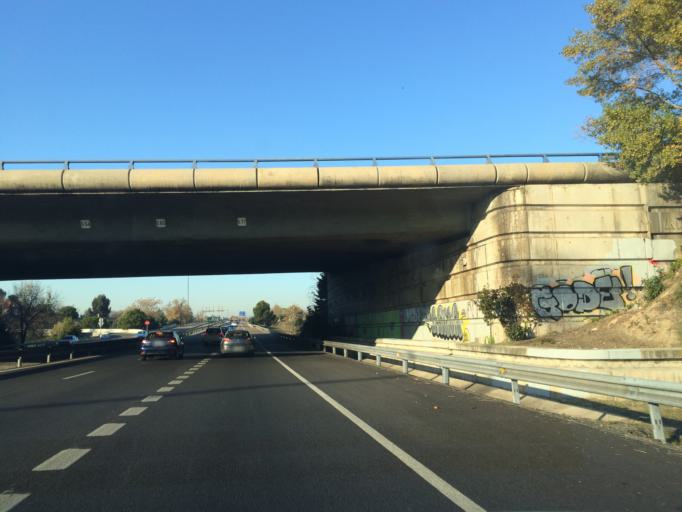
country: ES
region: Madrid
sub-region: Provincia de Madrid
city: Las Tablas
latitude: 40.5191
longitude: -3.6866
